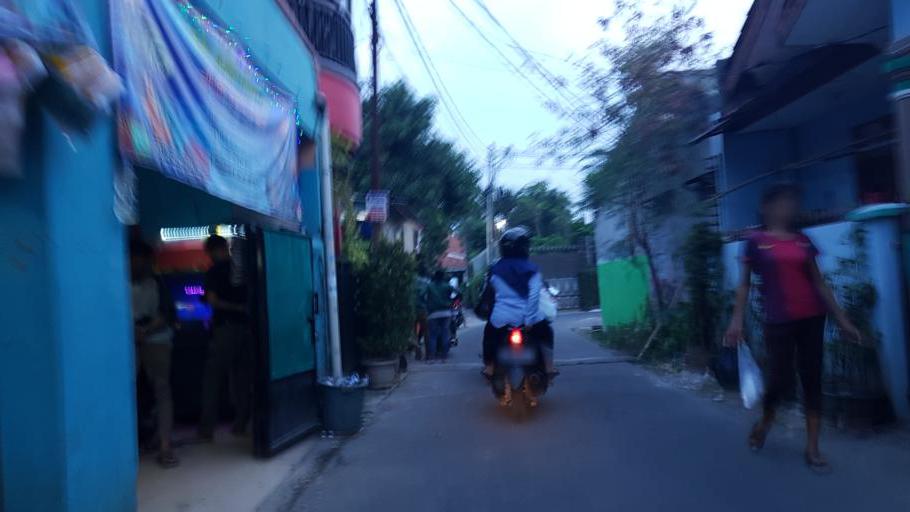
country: ID
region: West Java
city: Pamulang
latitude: -6.3252
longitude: 106.7939
